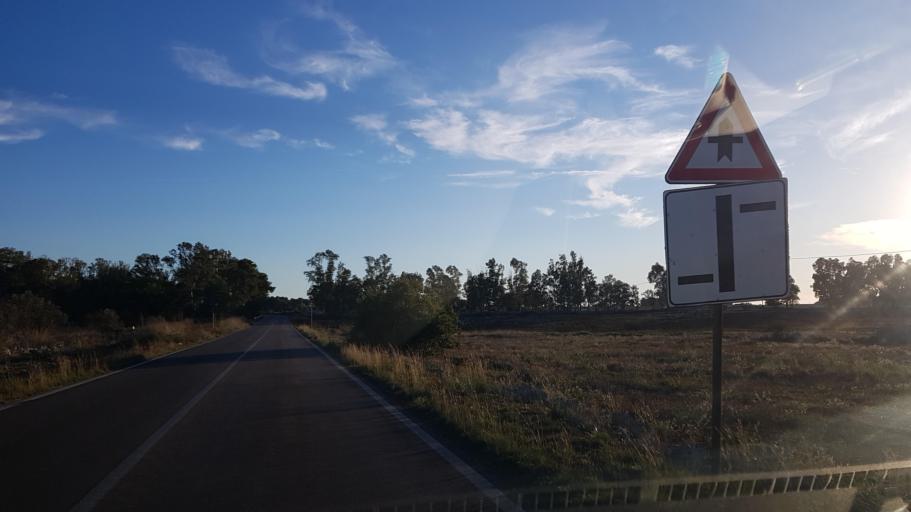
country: IT
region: Apulia
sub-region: Provincia di Lecce
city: Giorgilorio
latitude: 40.4050
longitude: 18.1981
